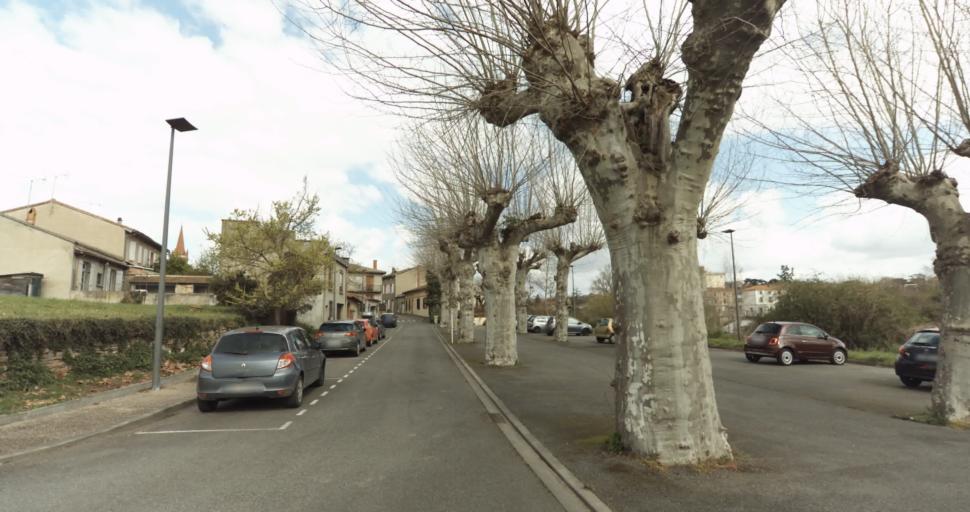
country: FR
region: Midi-Pyrenees
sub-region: Departement de la Haute-Garonne
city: Auterive
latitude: 43.3484
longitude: 1.4745
